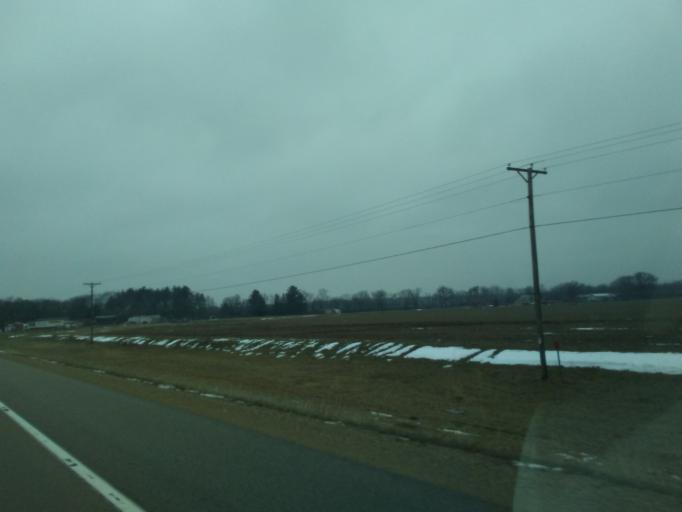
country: US
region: Wisconsin
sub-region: Sauk County
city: Spring Green
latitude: 43.1616
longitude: -90.0189
